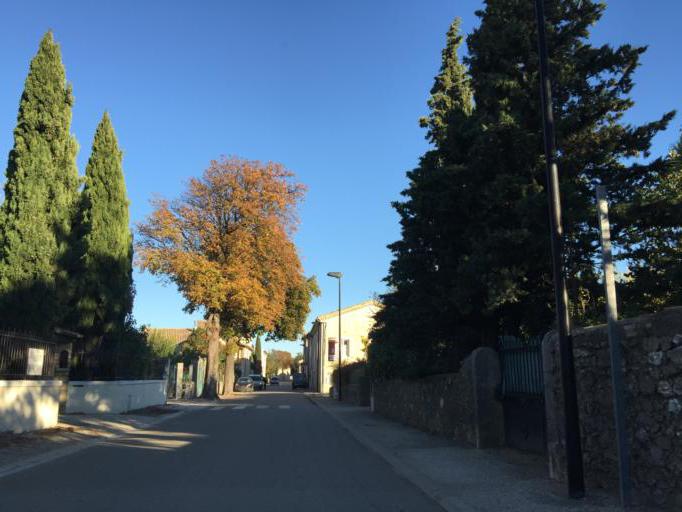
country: FR
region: Languedoc-Roussillon
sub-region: Departement du Gard
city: Saint-Julien-de-Peyrolas
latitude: 44.3934
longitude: 4.4996
